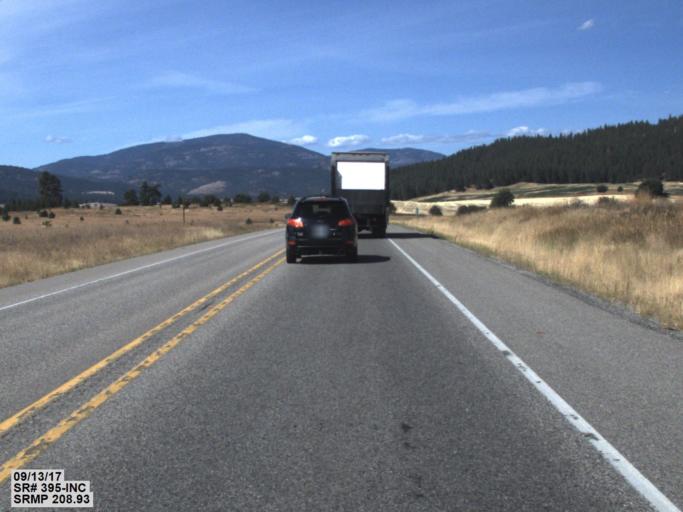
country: US
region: Washington
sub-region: Stevens County
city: Chewelah
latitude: 48.2928
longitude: -117.7397
